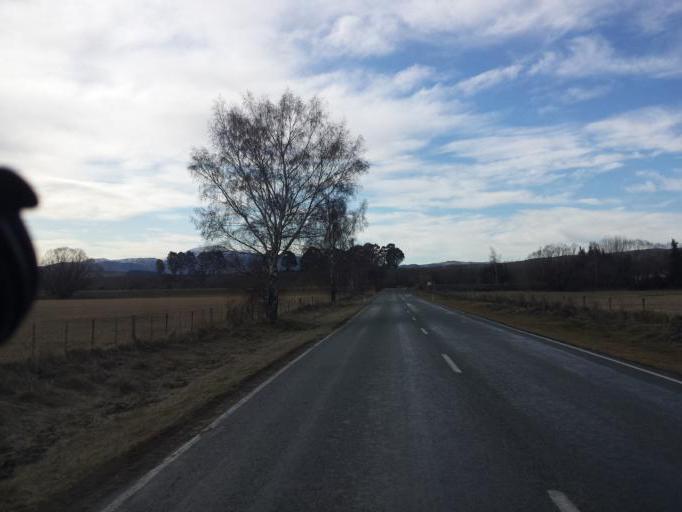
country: NZ
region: Canterbury
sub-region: Timaru District
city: Pleasant Point
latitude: -44.0932
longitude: 170.8427
